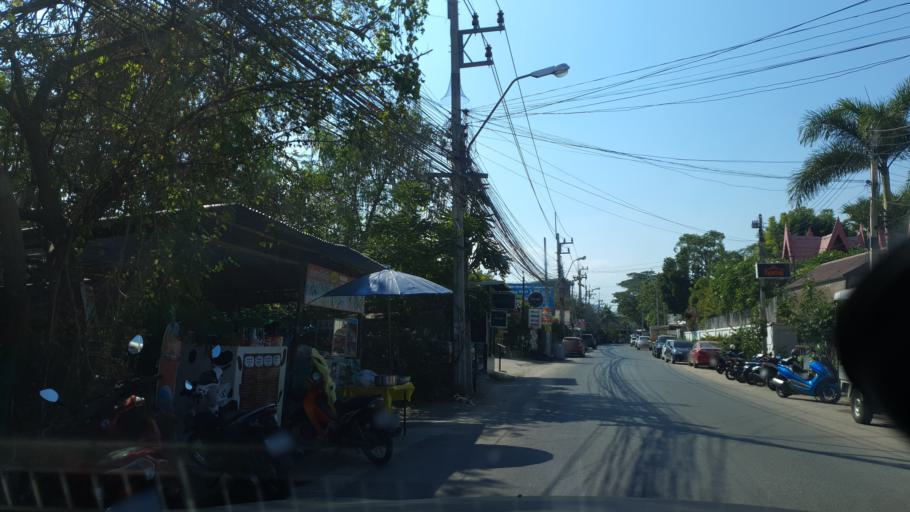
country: TH
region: Prachuap Khiri Khan
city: Hua Hin
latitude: 12.5544
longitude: 99.9568
